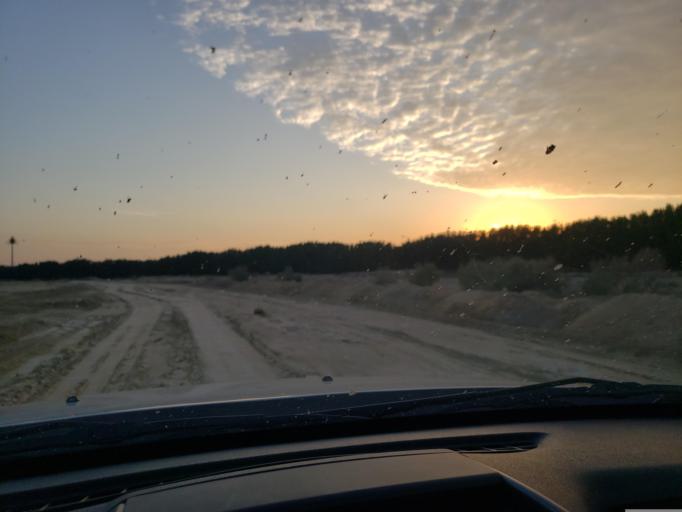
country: AE
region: Dubai
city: Dubai
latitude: 25.0192
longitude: 55.2625
